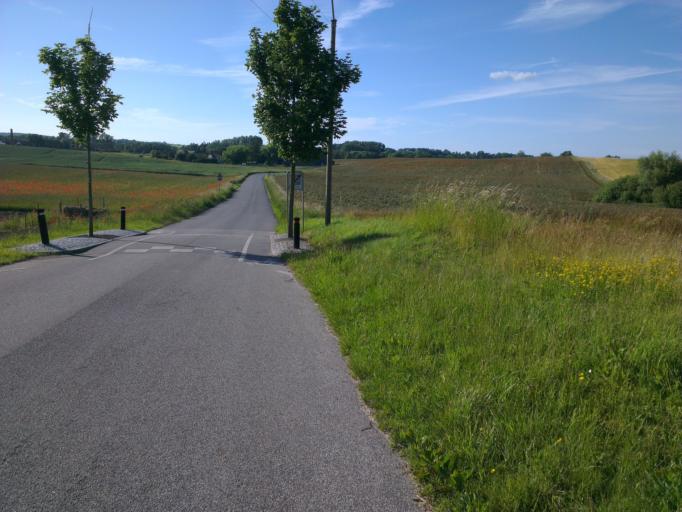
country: DK
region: Zealand
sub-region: Roskilde Kommune
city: Jyllinge
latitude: 55.7574
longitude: 12.0377
